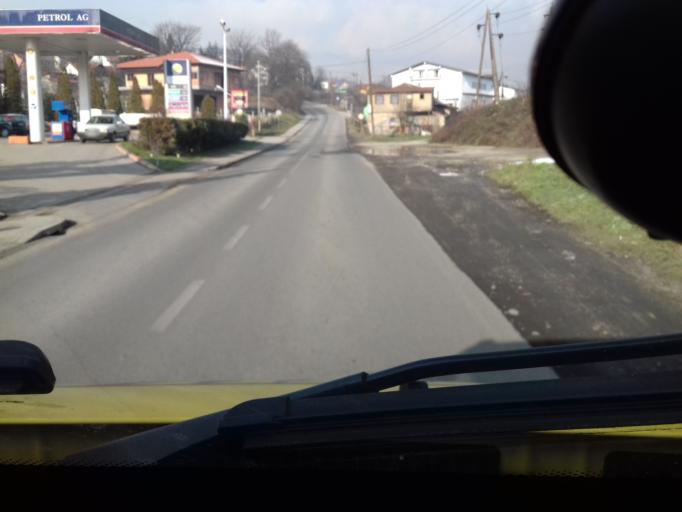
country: BA
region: Federation of Bosnia and Herzegovina
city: Zenica
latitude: 44.2097
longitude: 17.8952
